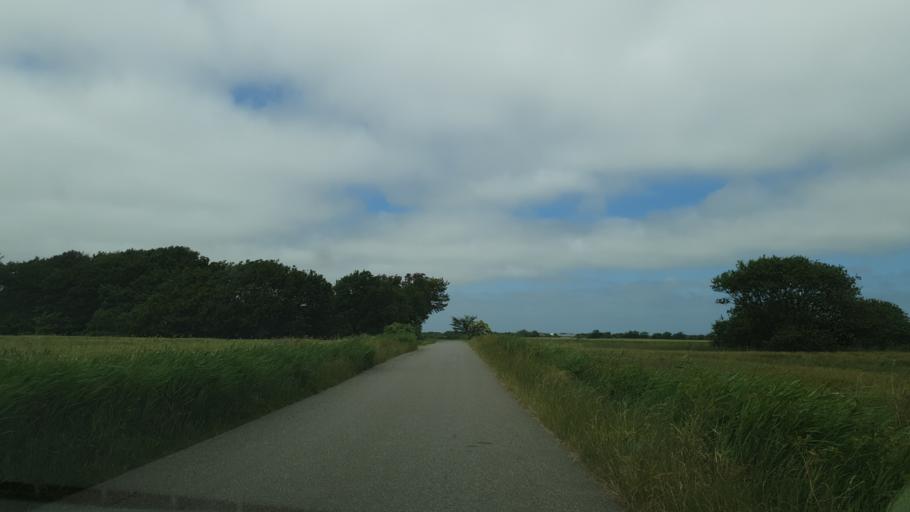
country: DK
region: Central Jutland
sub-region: Ringkobing-Skjern Kommune
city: Skjern
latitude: 55.9328
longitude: 8.4025
